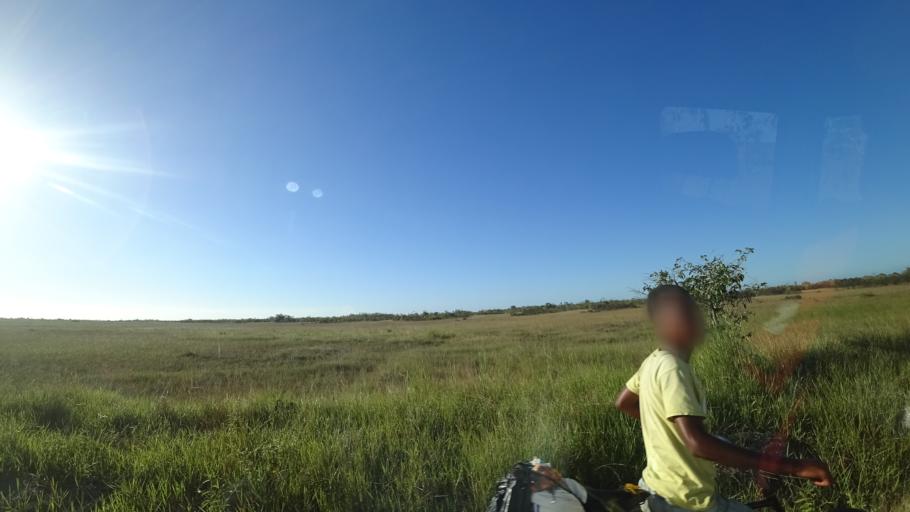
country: MZ
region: Sofala
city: Beira
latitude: -19.5790
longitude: 35.1703
